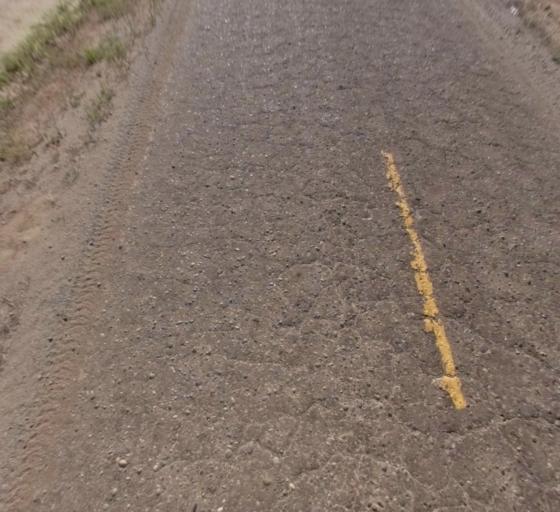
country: US
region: California
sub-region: Fresno County
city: Biola
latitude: 36.8296
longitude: -120.0368
